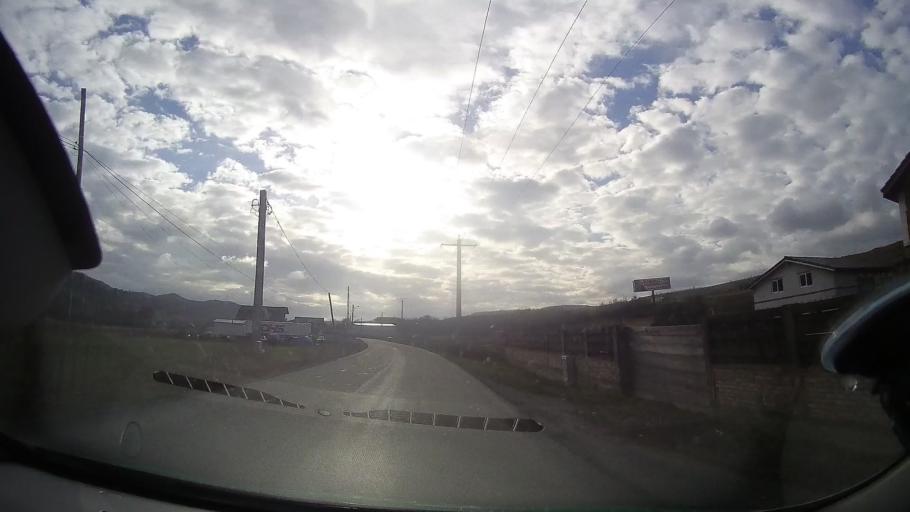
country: RO
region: Cluj
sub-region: Comuna Floresti
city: Luna de Sus
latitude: 46.7217
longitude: 23.4224
